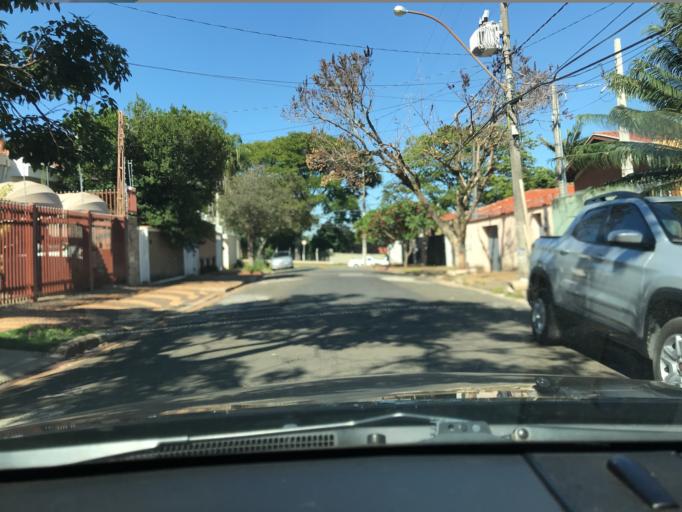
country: BR
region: Sao Paulo
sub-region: Campinas
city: Campinas
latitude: -22.8792
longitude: -47.0744
